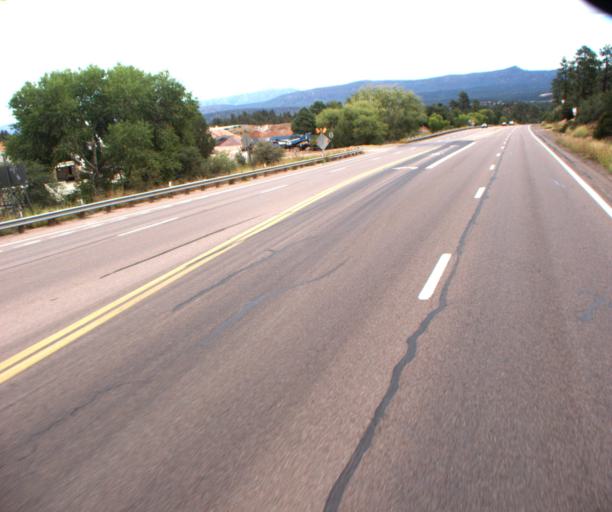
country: US
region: Arizona
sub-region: Gila County
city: Sun Valley
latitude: 34.2467
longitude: -111.2942
